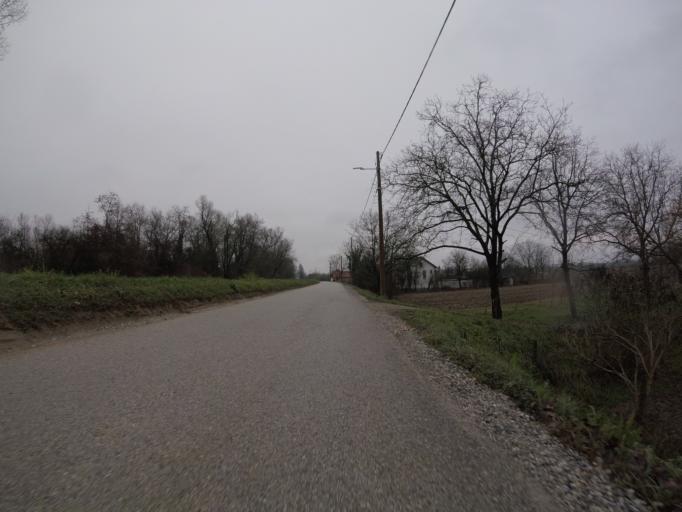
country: HR
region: Zagrebacka
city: Kuce
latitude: 45.6851
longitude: 16.2451
